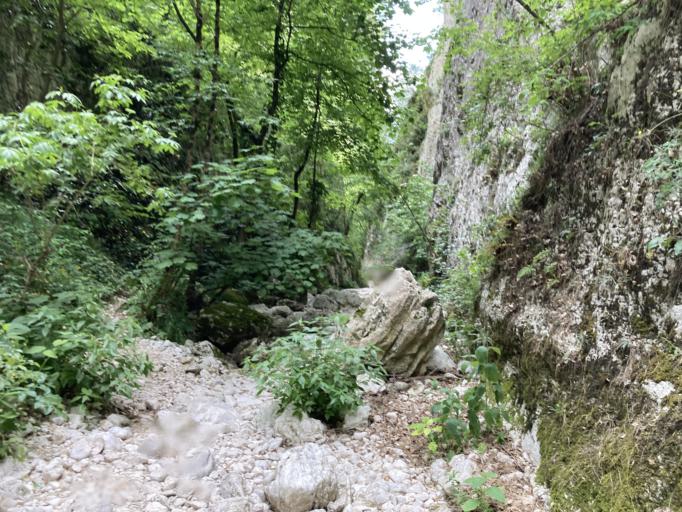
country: IT
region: Abruzzo
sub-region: Provincia dell' Aquila
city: Aielli
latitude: 42.1015
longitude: 13.5725
